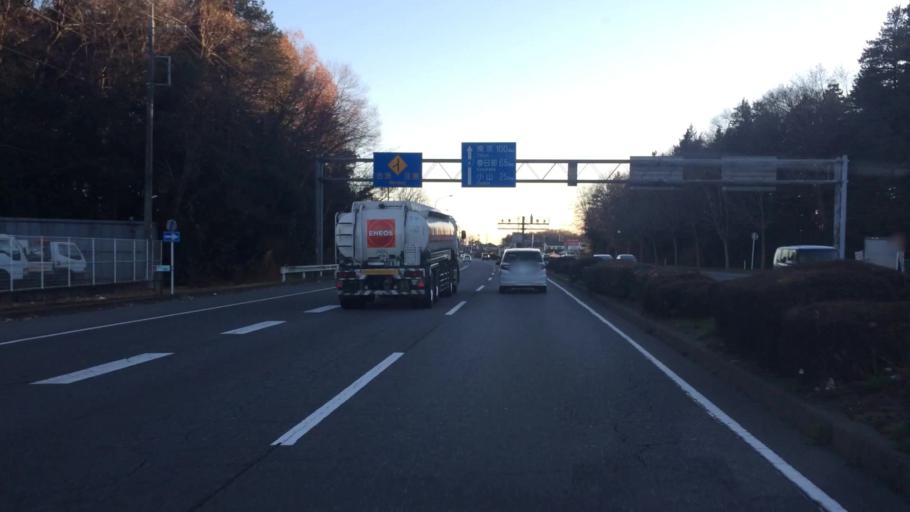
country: JP
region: Tochigi
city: Utsunomiya-shi
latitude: 36.5188
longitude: 139.9189
